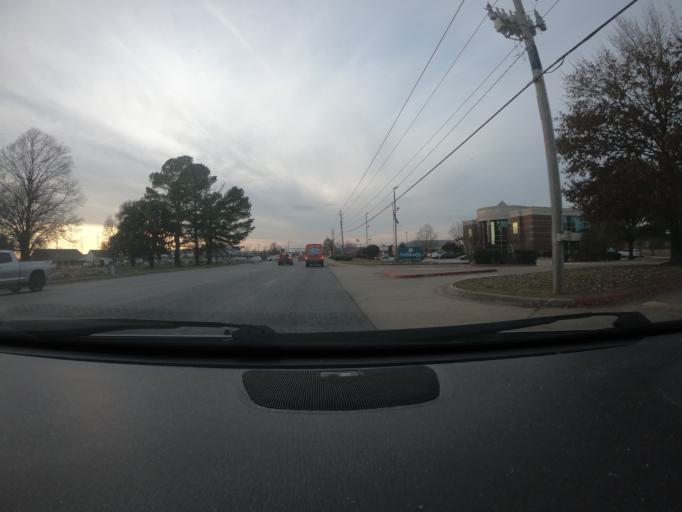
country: US
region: Arkansas
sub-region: Benton County
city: Bentonville
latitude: 36.3348
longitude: -94.1725
